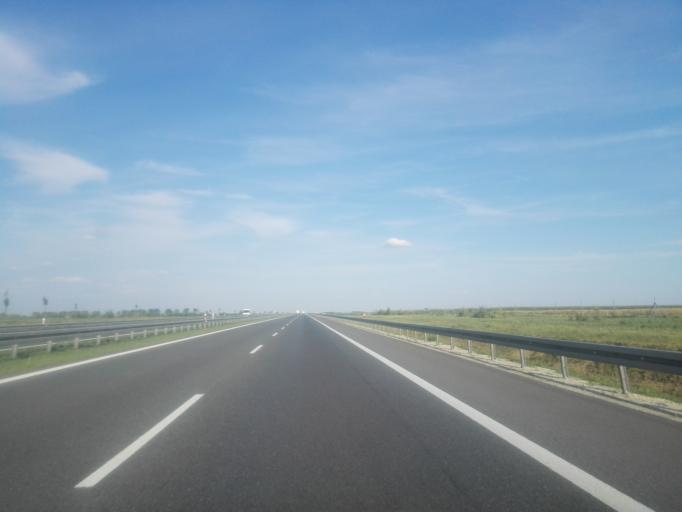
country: PL
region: Lower Silesian Voivodeship
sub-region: Powiat olesnicki
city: Dobroszyce
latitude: 51.2265
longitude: 17.2742
